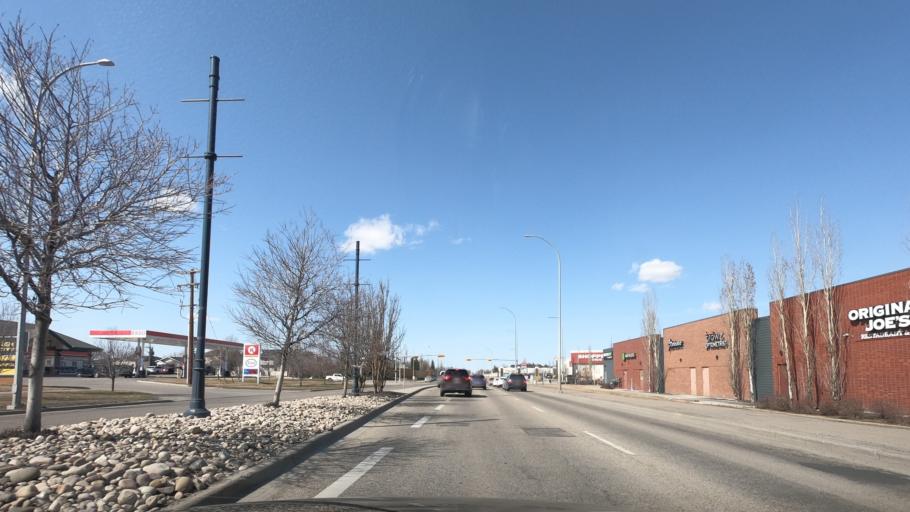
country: CA
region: Alberta
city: Airdrie
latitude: 51.2917
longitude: -114.0251
